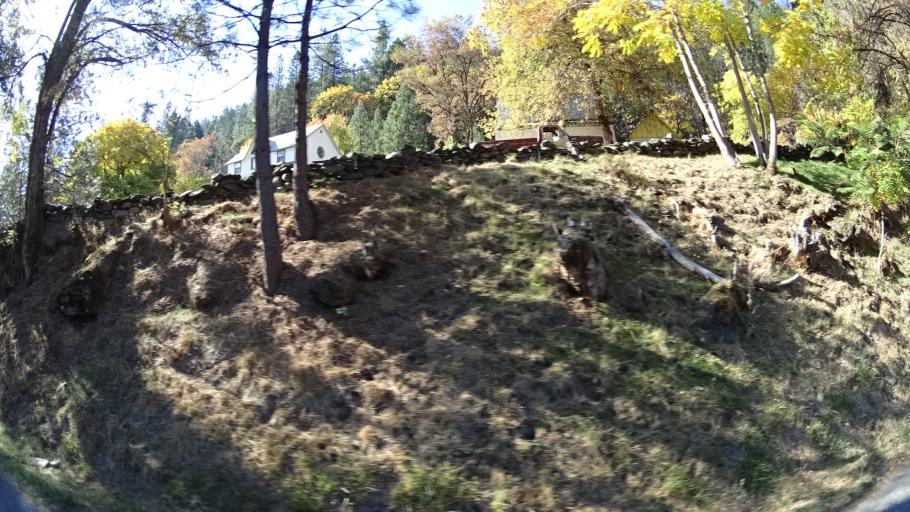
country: US
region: California
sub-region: Siskiyou County
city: Happy Camp
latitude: 41.7480
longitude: -123.0098
